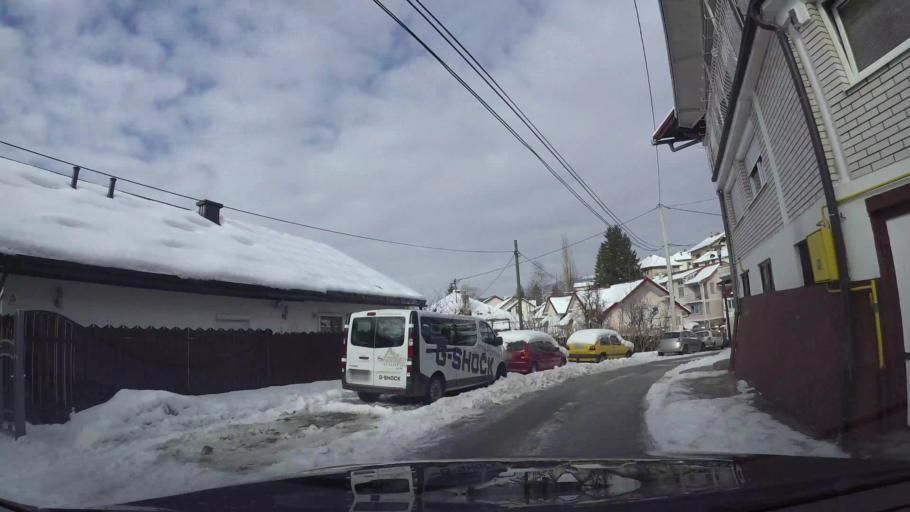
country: BA
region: Federation of Bosnia and Herzegovina
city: Kobilja Glava
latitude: 43.8747
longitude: 18.4156
